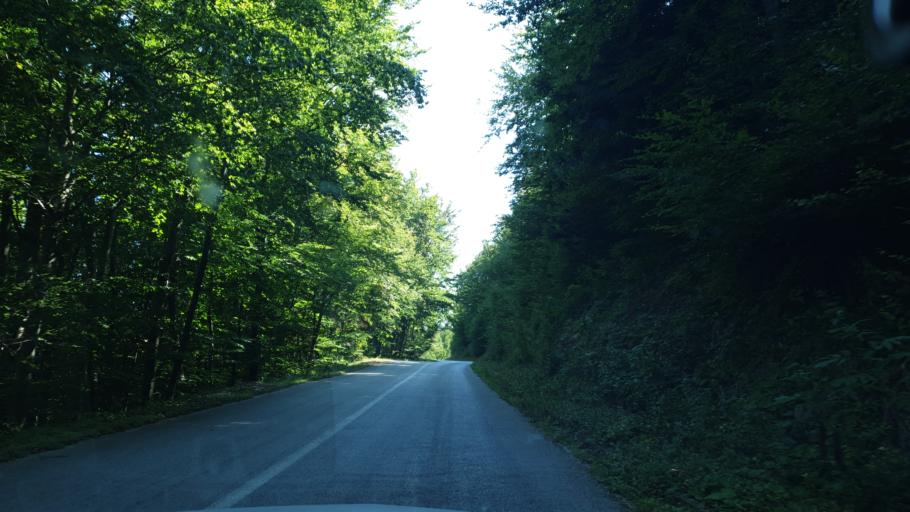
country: RS
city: Zlatibor
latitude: 43.6606
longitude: 19.8283
